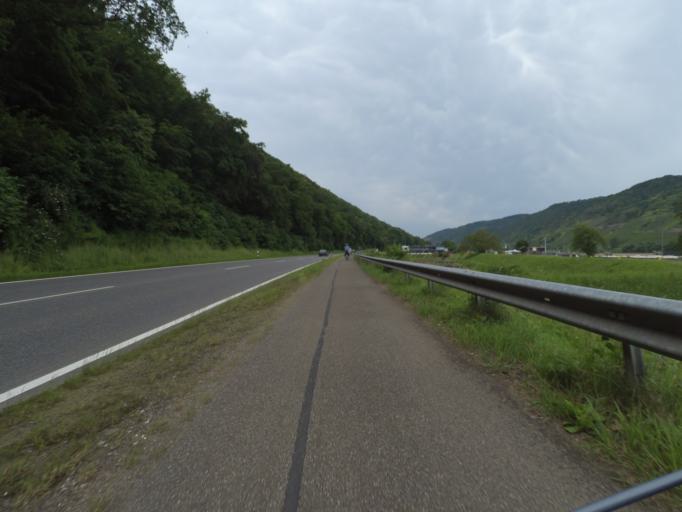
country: DE
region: Rheinland-Pfalz
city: Lutz
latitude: 50.1818
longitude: 7.3366
